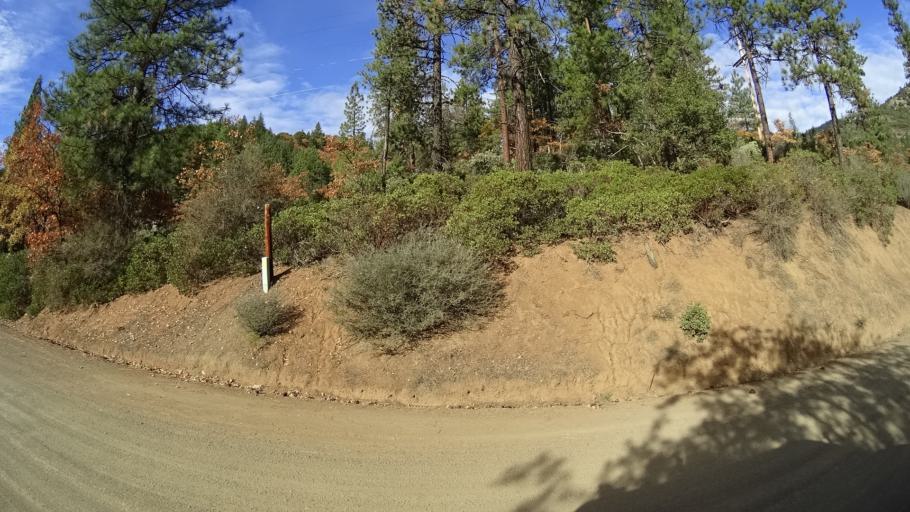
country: US
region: California
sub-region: Siskiyou County
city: Yreka
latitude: 41.7078
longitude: -122.8147
